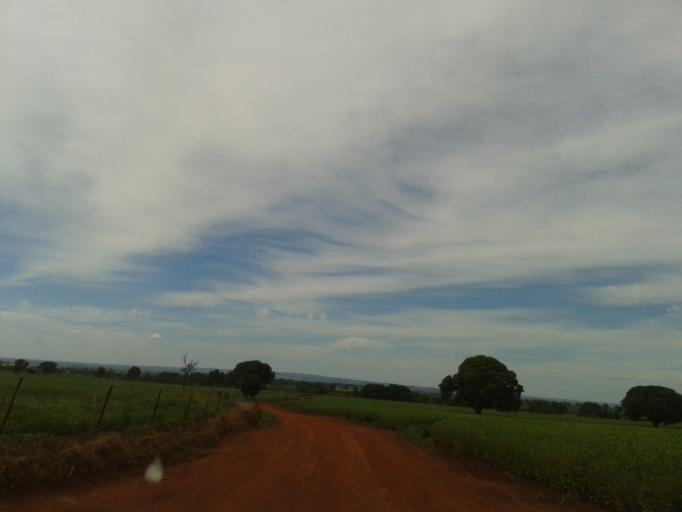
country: BR
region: Minas Gerais
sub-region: Capinopolis
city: Capinopolis
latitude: -18.7419
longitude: -49.8449
